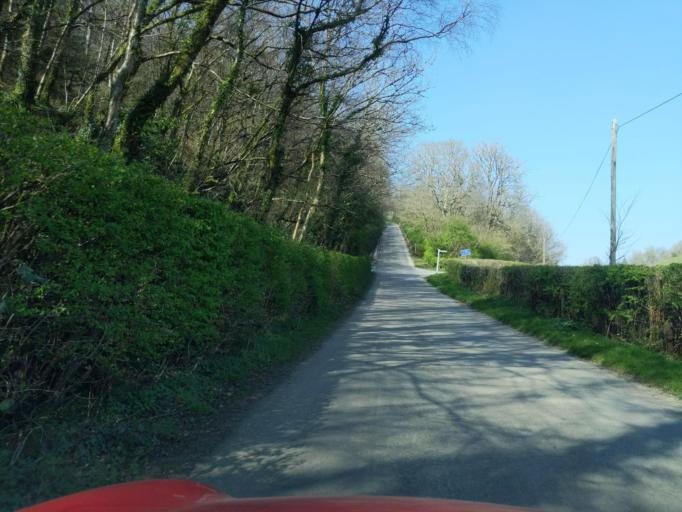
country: GB
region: England
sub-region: Devon
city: Horrabridge
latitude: 50.4678
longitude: -4.1339
